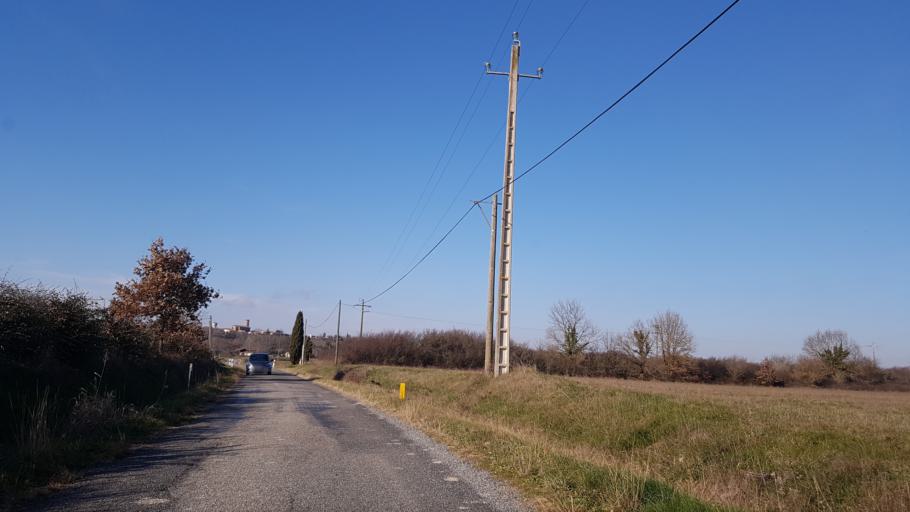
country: FR
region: Midi-Pyrenees
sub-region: Departement de l'Ariege
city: Mazeres
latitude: 43.1800
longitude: 1.6533
